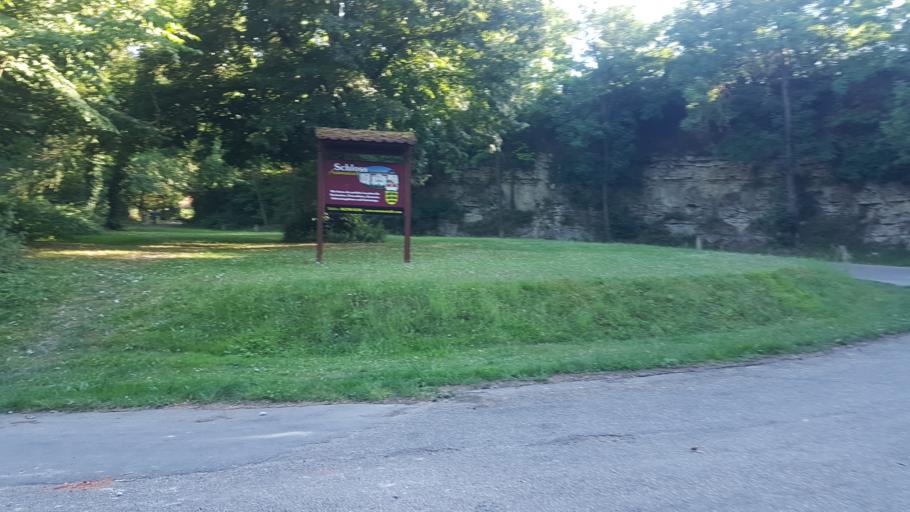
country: DE
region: Baden-Wuerttemberg
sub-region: Regierungsbezirk Stuttgart
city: Mockmuhl
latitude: 49.2956
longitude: 9.3266
